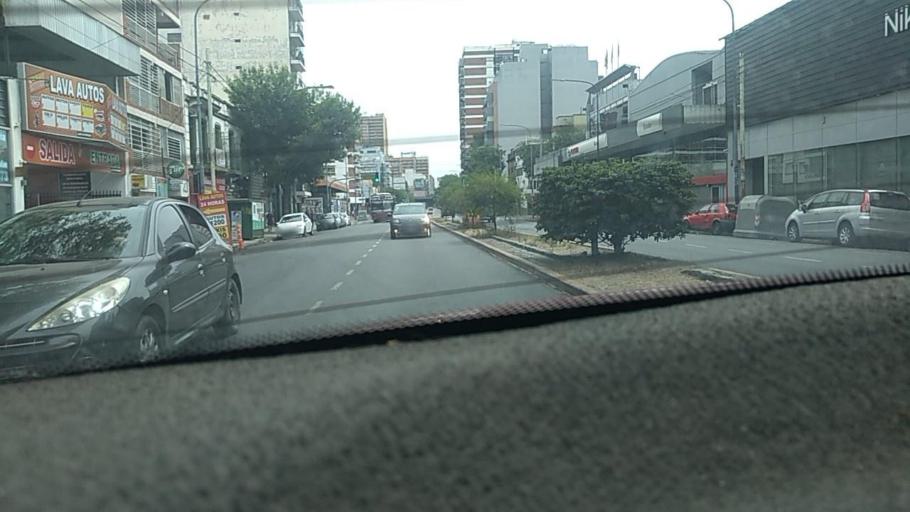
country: AR
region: Buenos Aires F.D.
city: Villa Santa Rita
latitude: -34.6358
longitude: -58.4902
